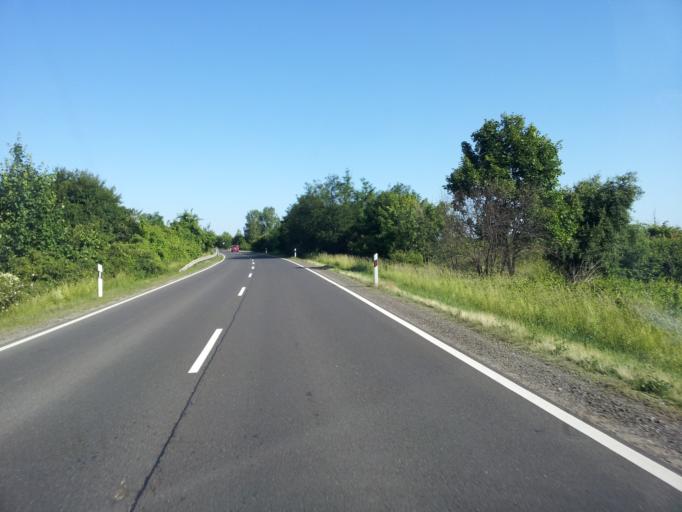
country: HU
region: Nograd
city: Nagyoroszi
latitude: 48.0220
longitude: 19.0718
